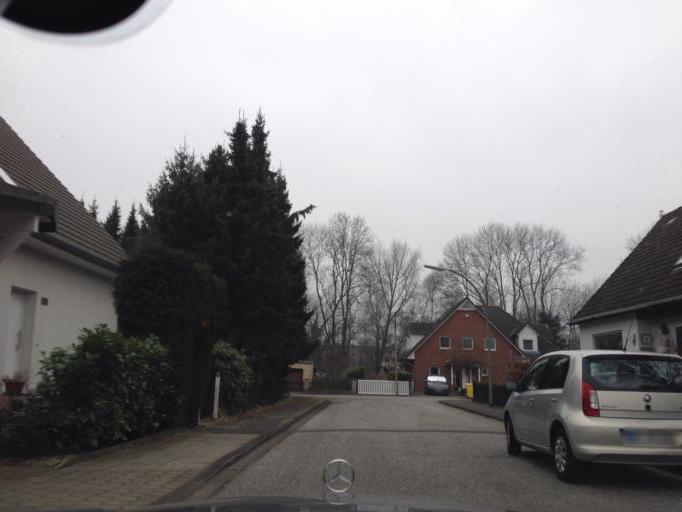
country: DE
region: Hamburg
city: Farmsen-Berne
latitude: 53.6020
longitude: 10.0989
